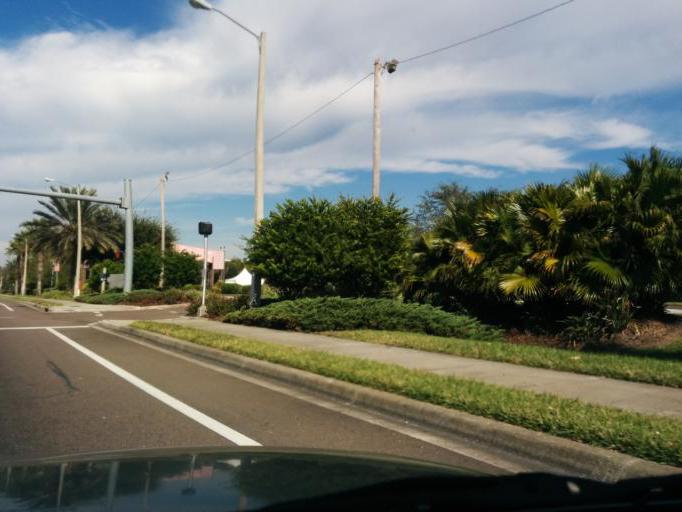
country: US
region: Florida
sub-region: Hillsborough County
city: Temple Terrace
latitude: 28.0378
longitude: -82.4162
